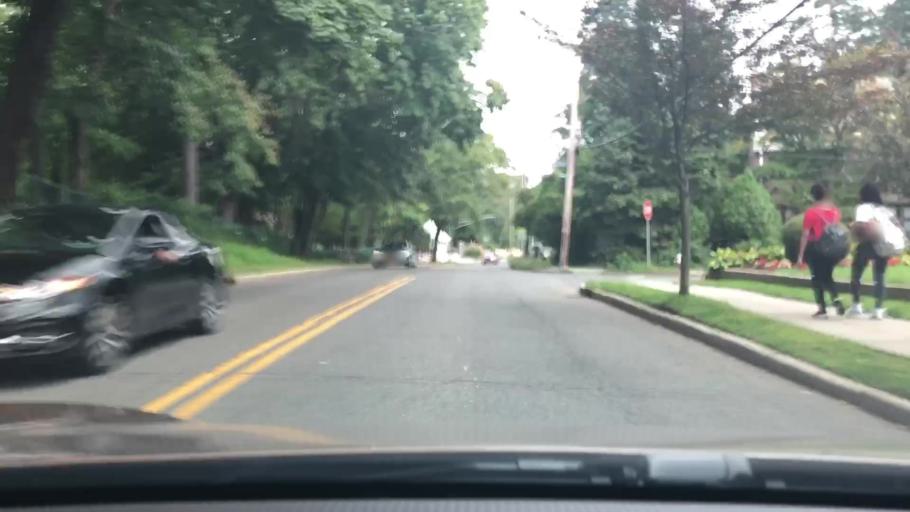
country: US
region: New York
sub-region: Westchester County
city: Bronxville
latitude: 40.9264
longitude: -73.8183
